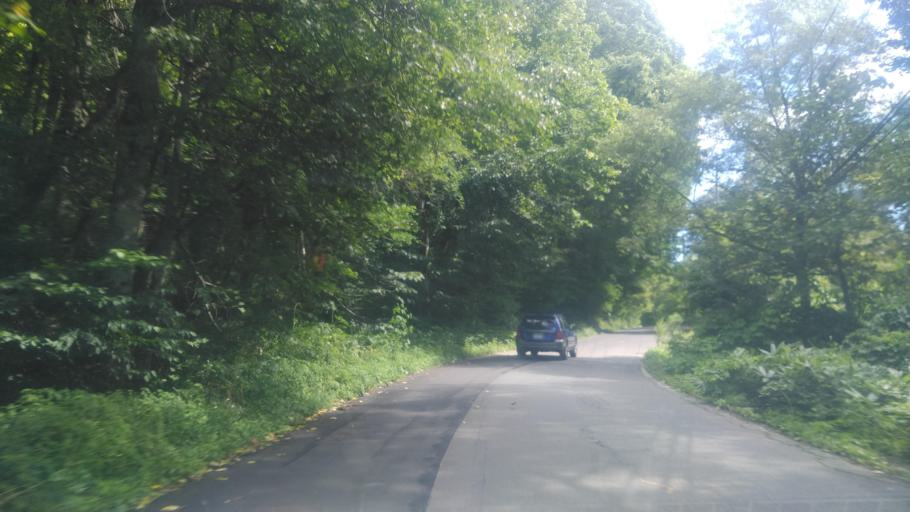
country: JP
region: Nagano
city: Nagano-shi
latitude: 36.8276
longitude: 138.1794
